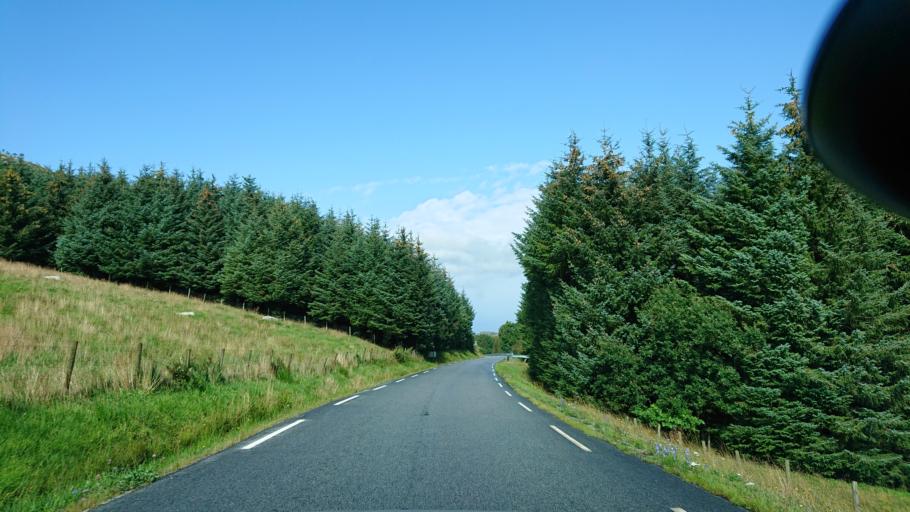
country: NO
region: Rogaland
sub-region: Gjesdal
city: Algard
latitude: 58.6887
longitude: 5.8751
